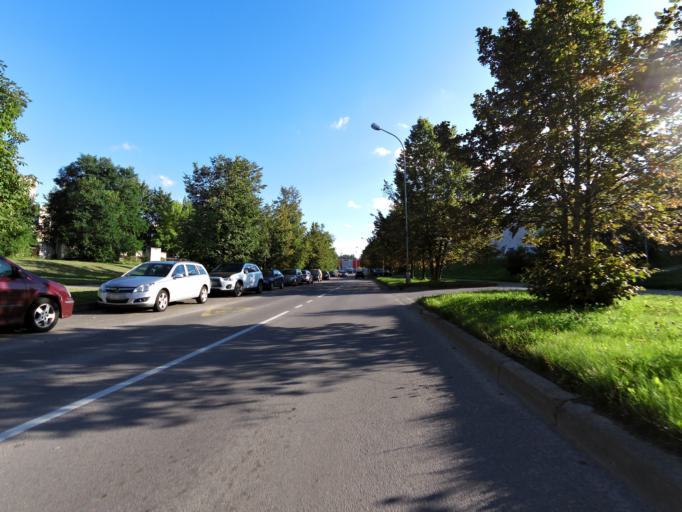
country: LT
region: Vilnius County
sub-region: Vilnius
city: Fabijoniskes
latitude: 54.7238
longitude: 25.2448
